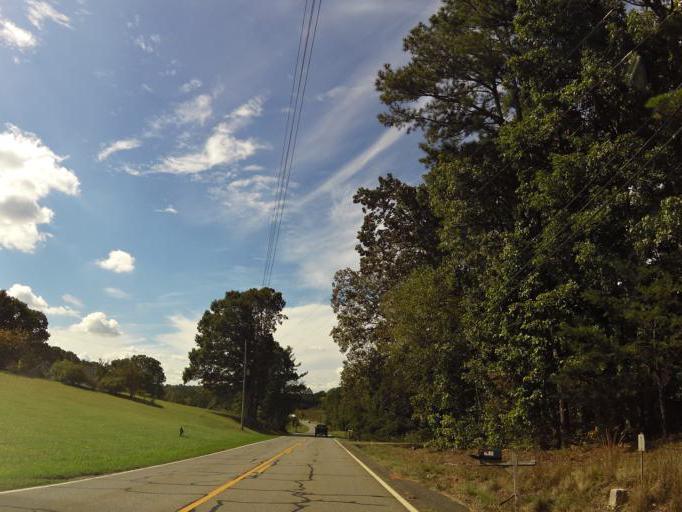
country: US
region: Georgia
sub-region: Pickens County
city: Nelson
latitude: 34.4175
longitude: -84.3070
